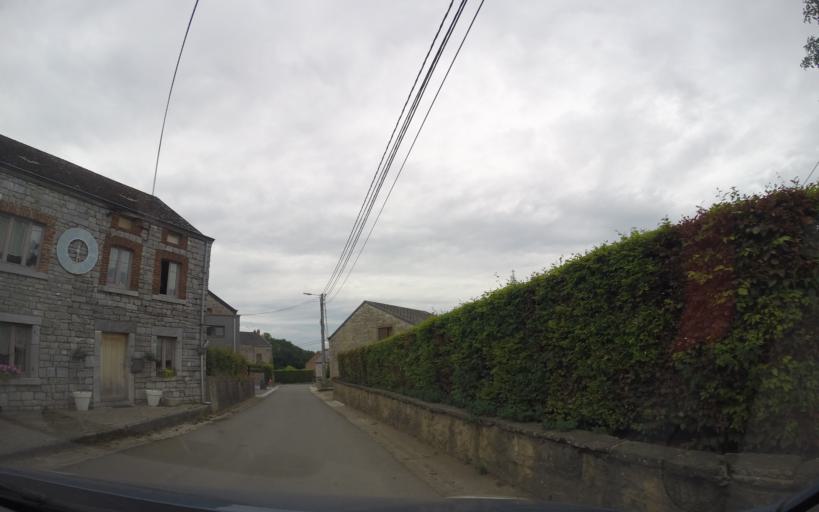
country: BE
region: Wallonia
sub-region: Province du Luxembourg
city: Durbuy
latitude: 50.3656
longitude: 5.4655
